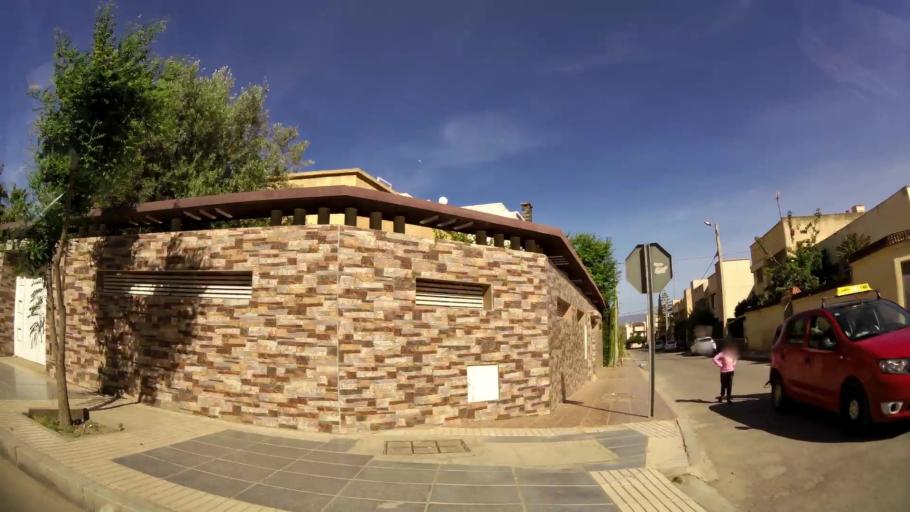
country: MA
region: Oriental
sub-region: Oujda-Angad
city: Oujda
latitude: 34.6694
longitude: -1.9121
